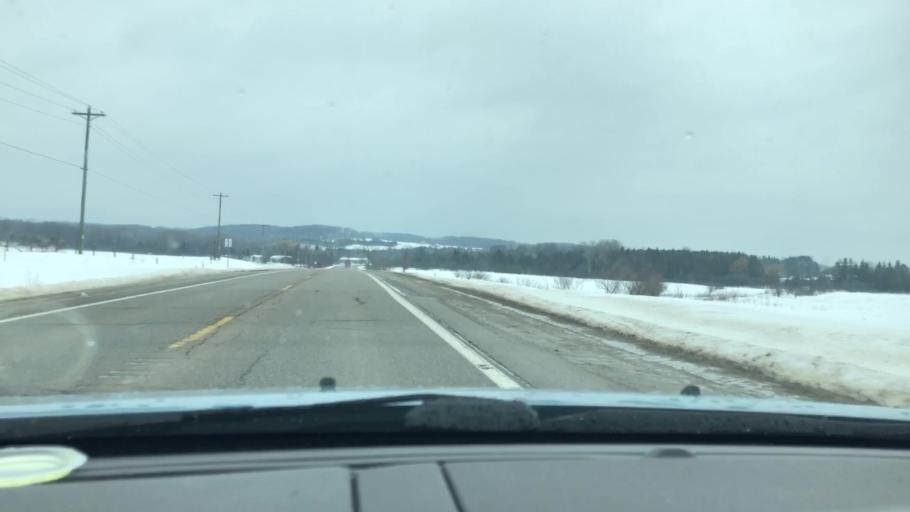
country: US
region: Michigan
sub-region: Charlevoix County
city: East Jordan
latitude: 45.1251
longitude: -85.1339
